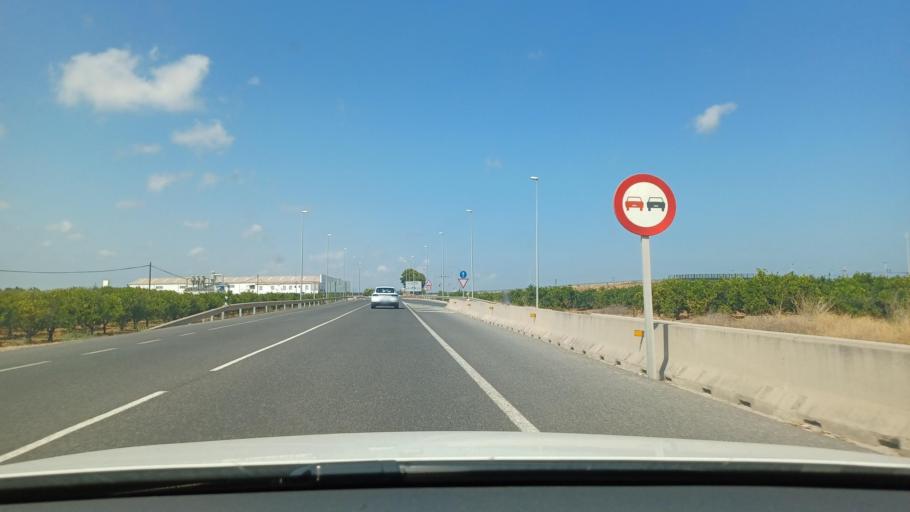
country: ES
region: Valencia
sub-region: Provincia de Castello
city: Chilches
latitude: 39.8005
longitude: -0.1770
